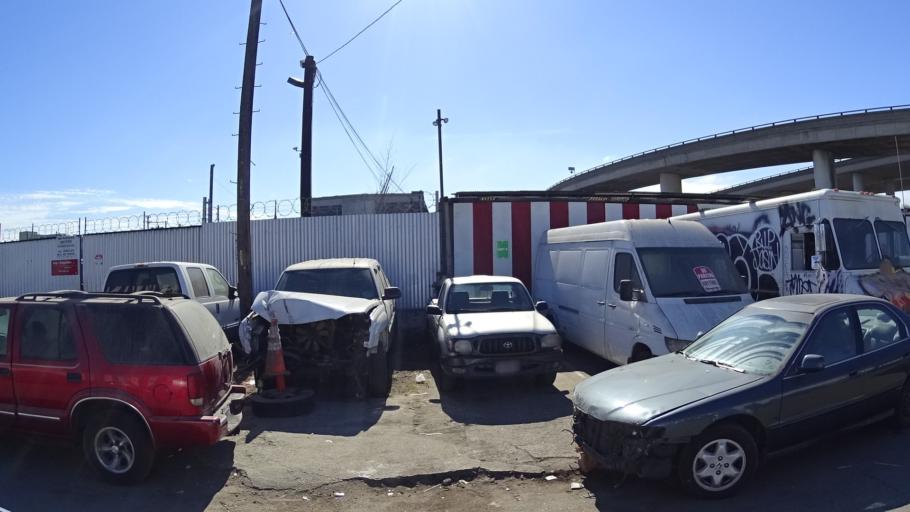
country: US
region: California
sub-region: San Francisco County
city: San Francisco
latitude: 37.7464
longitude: -122.3927
